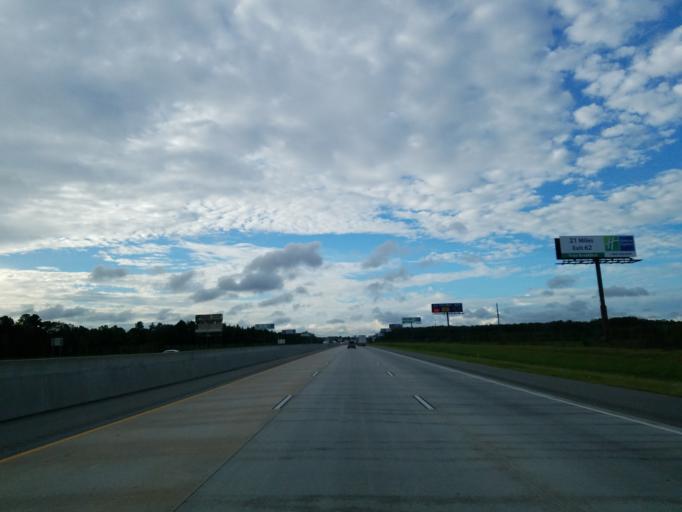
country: US
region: Georgia
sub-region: Cook County
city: Sparks
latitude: 31.1490
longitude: -83.4437
